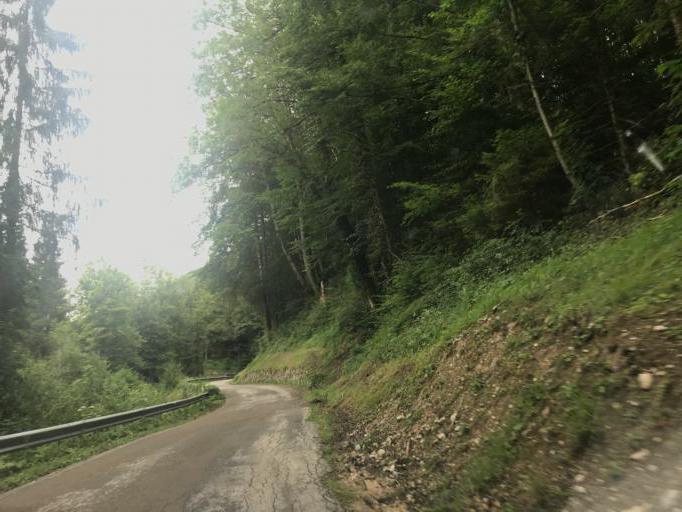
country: FR
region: Franche-Comte
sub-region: Departement du Jura
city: Saint-Claude
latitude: 46.3414
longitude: 5.8368
